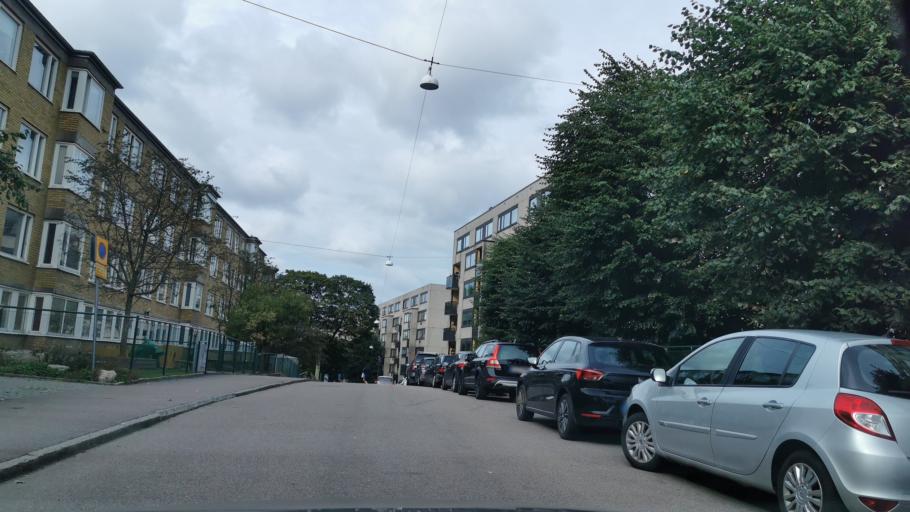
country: SE
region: Vaestra Goetaland
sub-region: Goteborg
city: Goeteborg
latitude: 57.6916
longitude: 11.9468
